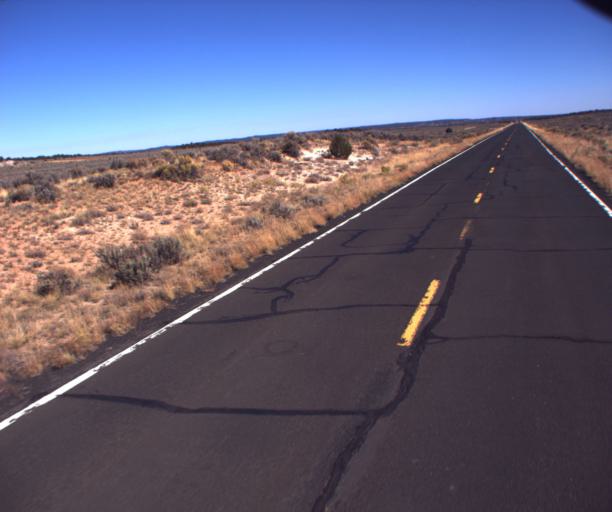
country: US
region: Arizona
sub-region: Navajo County
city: First Mesa
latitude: 35.7550
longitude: -110.0270
